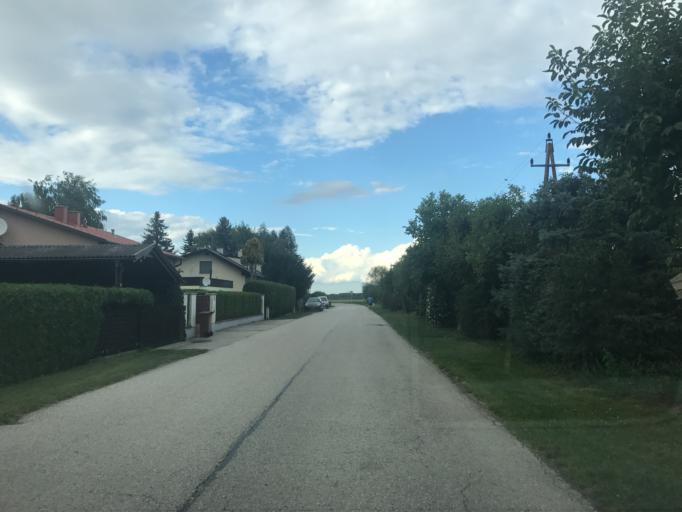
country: AT
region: Burgenland
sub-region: Eisenstadt-Umgebung
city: Neufeld an der Leitha
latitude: 47.8747
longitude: 16.3992
